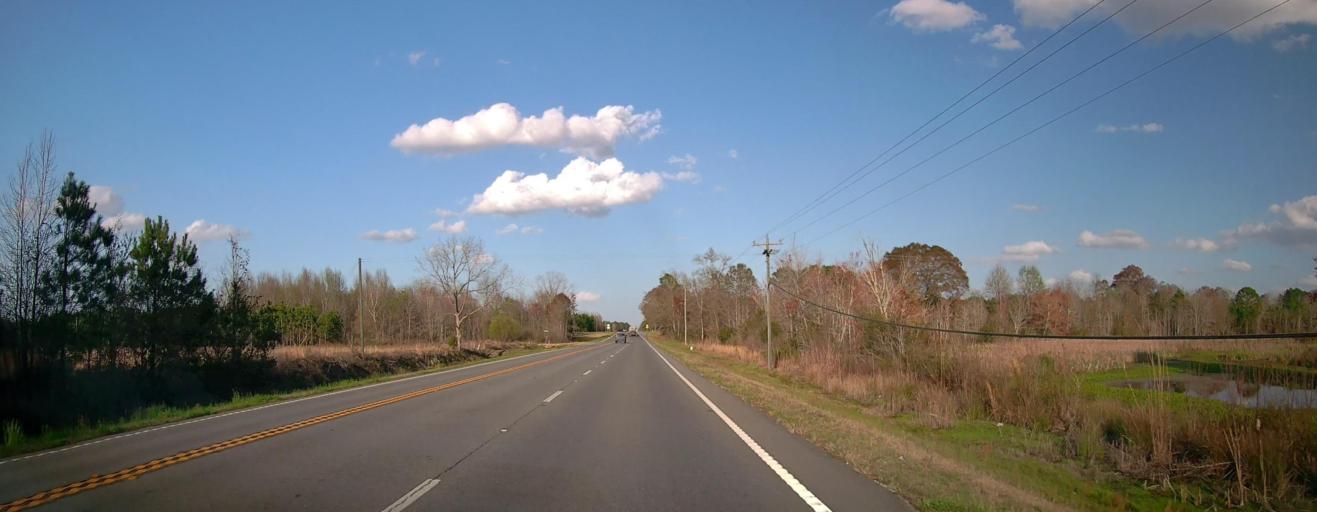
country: US
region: Georgia
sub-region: Tattnall County
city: Reidsville
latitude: 32.1137
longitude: -82.0793
